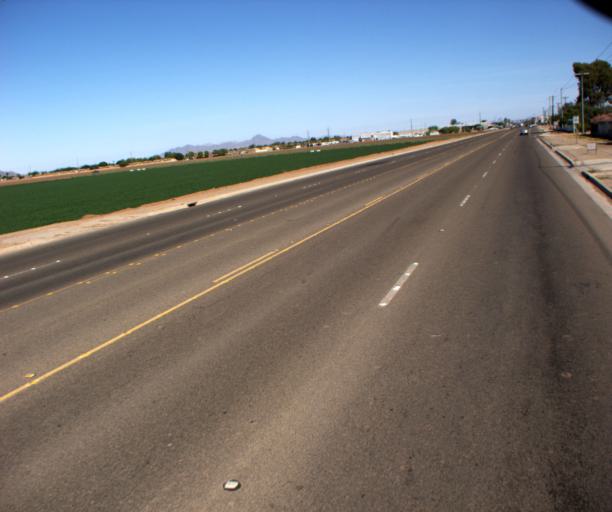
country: US
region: Arizona
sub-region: Yuma County
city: Yuma
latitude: 32.6637
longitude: -114.6501
